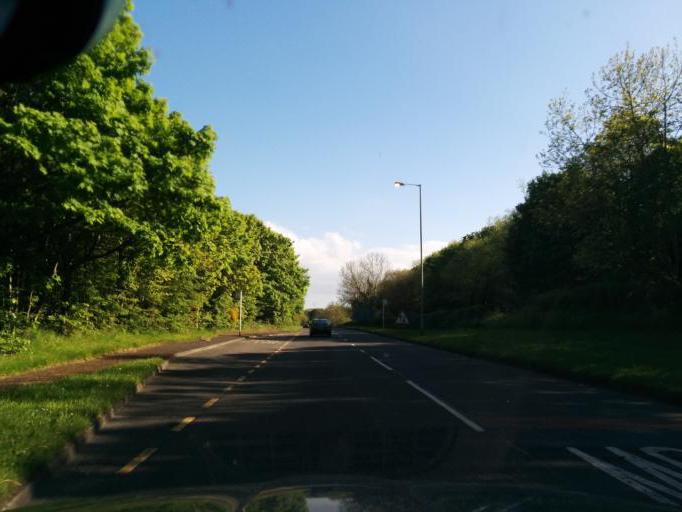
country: GB
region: England
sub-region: Northumberland
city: Cramlington
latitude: 55.1017
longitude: -1.5959
